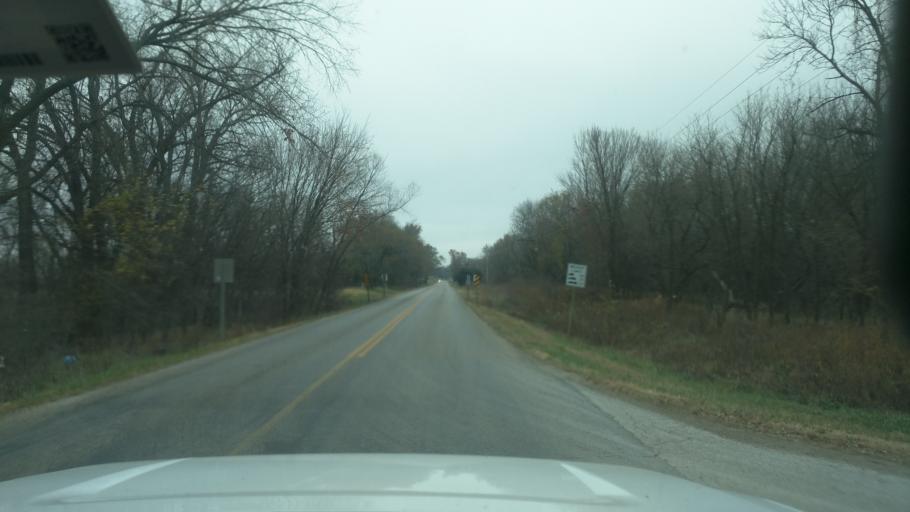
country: US
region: Kansas
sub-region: Lyon County
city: Emporia
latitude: 38.5210
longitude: -96.2617
